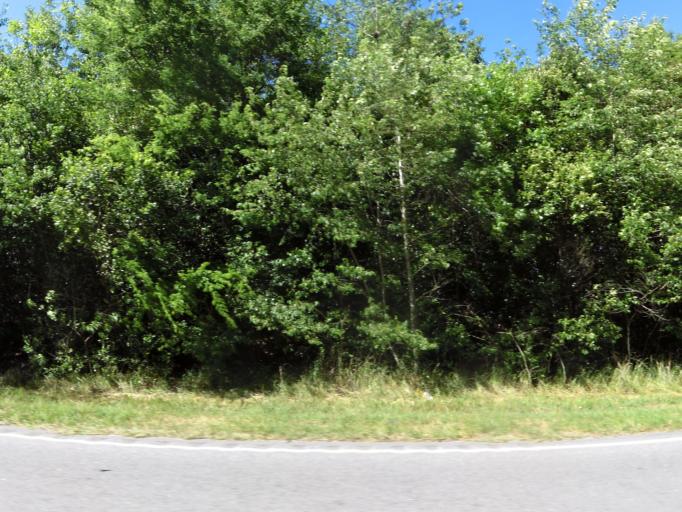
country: US
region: South Carolina
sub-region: Barnwell County
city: Williston
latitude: 33.3778
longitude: -81.3695
